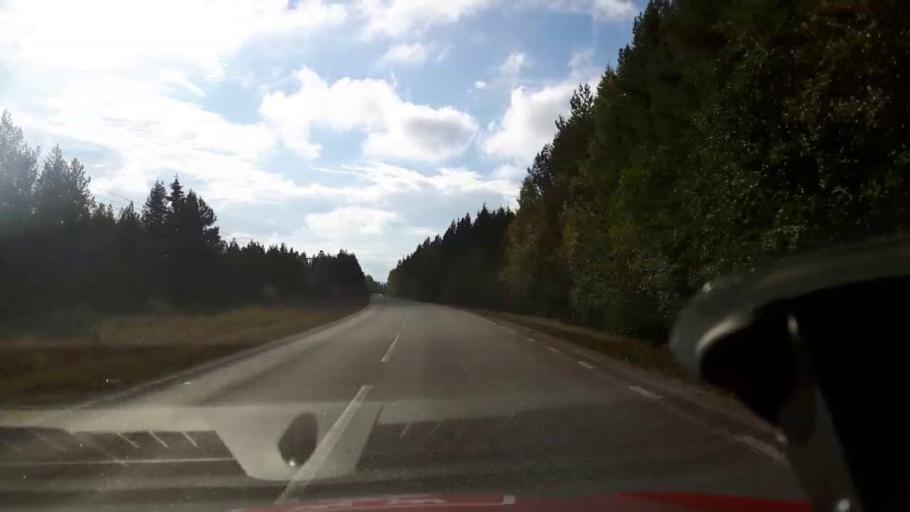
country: SE
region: Vaesternorrland
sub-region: Ange Kommun
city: Ange
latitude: 62.0846
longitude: 15.0951
